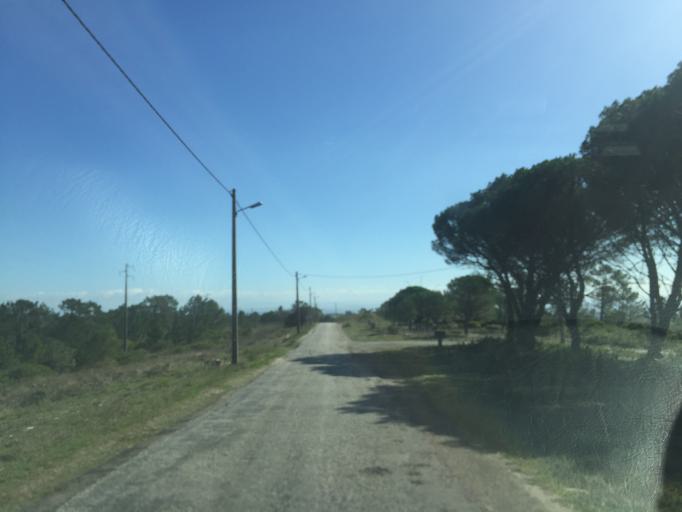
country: PT
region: Coimbra
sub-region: Figueira da Foz
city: Tavarede
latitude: 40.1917
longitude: -8.8392
